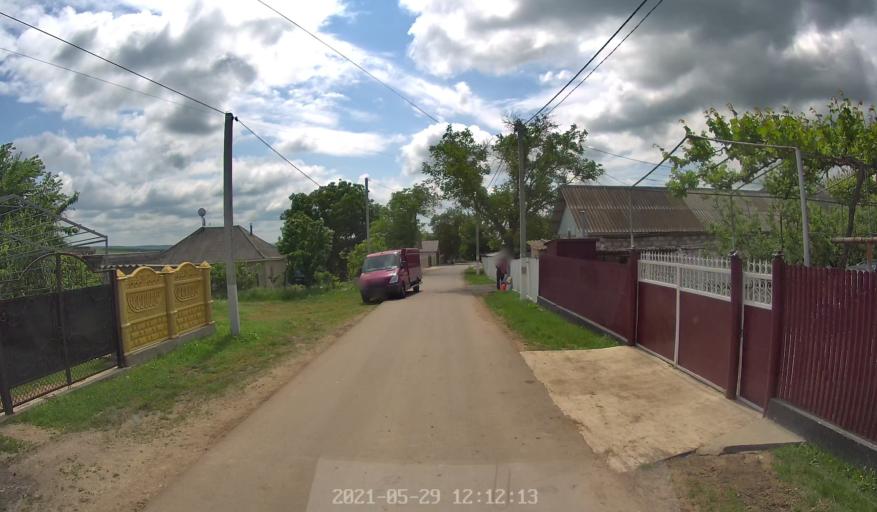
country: MD
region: Hincesti
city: Hincesti
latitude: 46.8800
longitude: 28.6315
